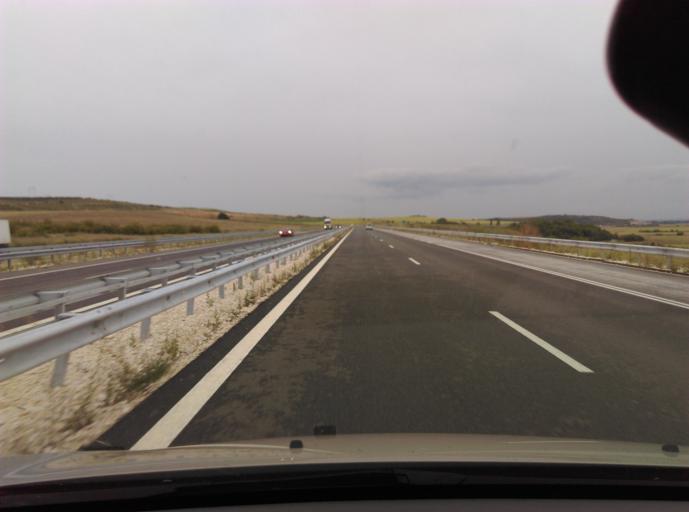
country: BG
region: Stara Zagora
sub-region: Obshtina Chirpan
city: Chirpan
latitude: 42.1187
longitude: 25.3904
